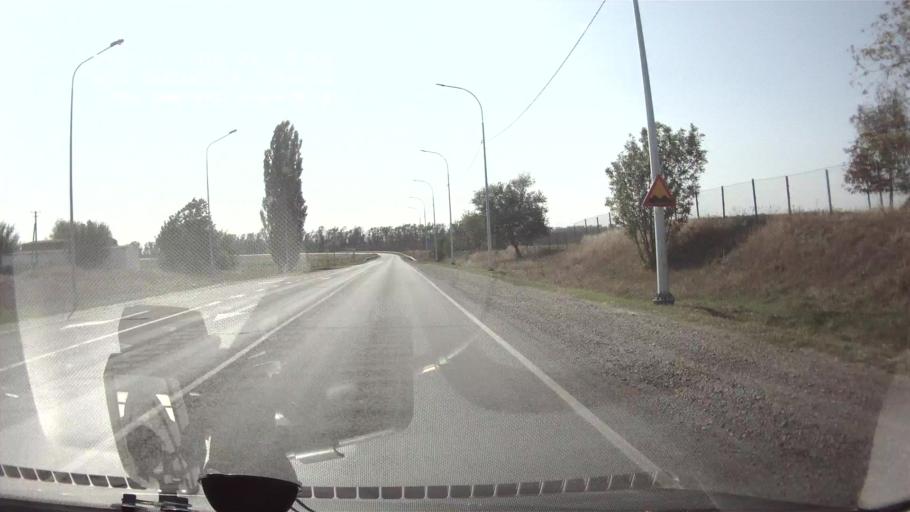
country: RU
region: Krasnodarskiy
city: Dmitriyevskaya
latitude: 45.7067
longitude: 40.7273
